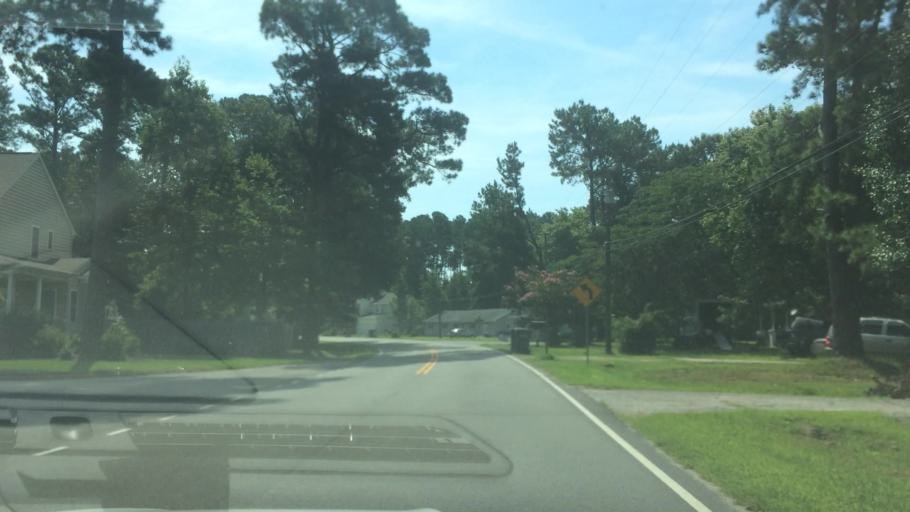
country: US
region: Virginia
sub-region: City of Poquoson
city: Poquoson
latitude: 37.1629
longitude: -76.4267
